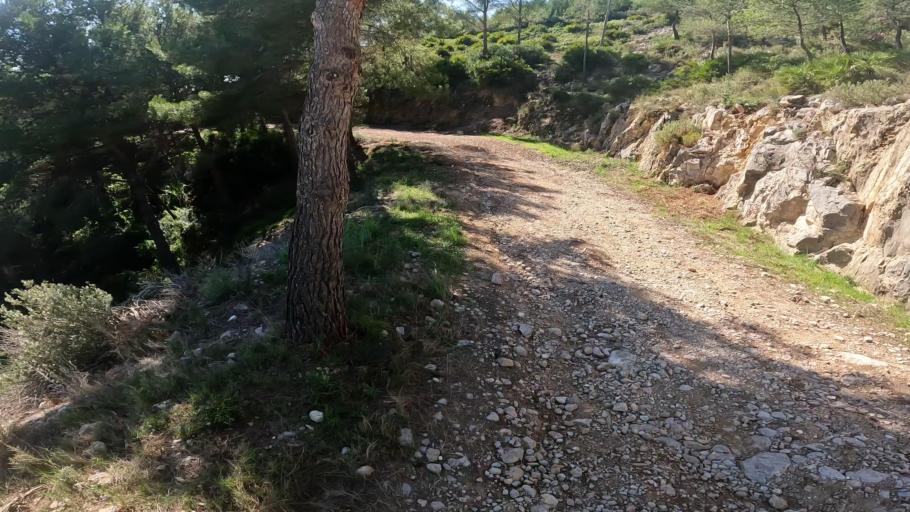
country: ES
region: Valencia
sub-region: Provincia de Castello
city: Alcoceber
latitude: 40.2660
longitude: 0.2721
